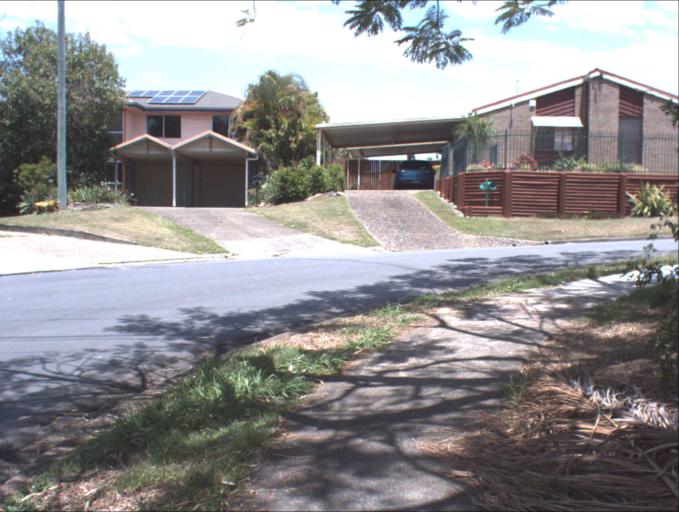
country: AU
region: Queensland
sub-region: Logan
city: Rochedale South
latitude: -27.5923
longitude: 153.1416
